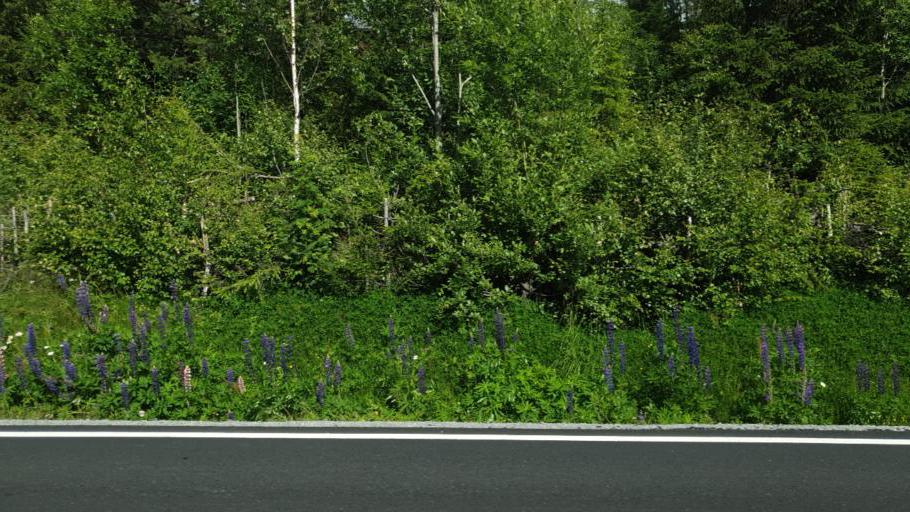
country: NO
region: Oppland
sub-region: Oystre Slidre
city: Heggenes
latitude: 61.1719
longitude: 8.9944
